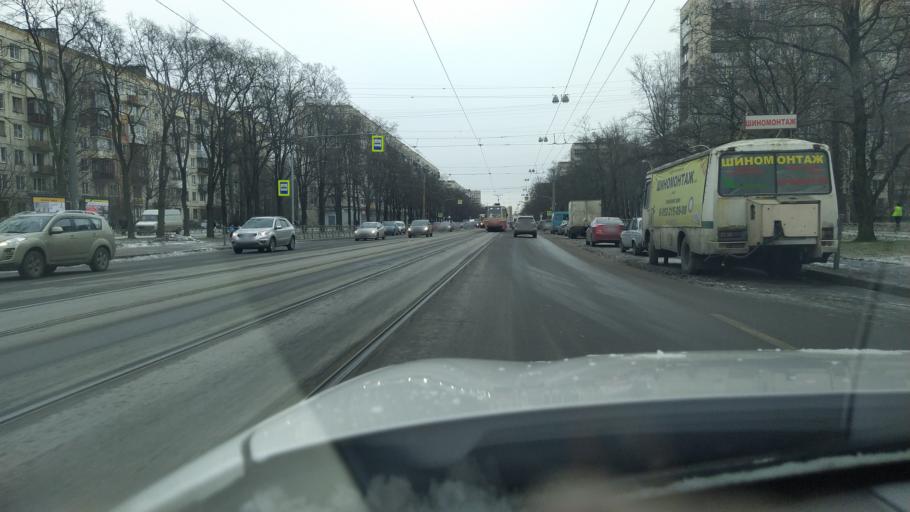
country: RU
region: Leningrad
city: Akademicheskoe
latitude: 60.0102
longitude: 30.4092
